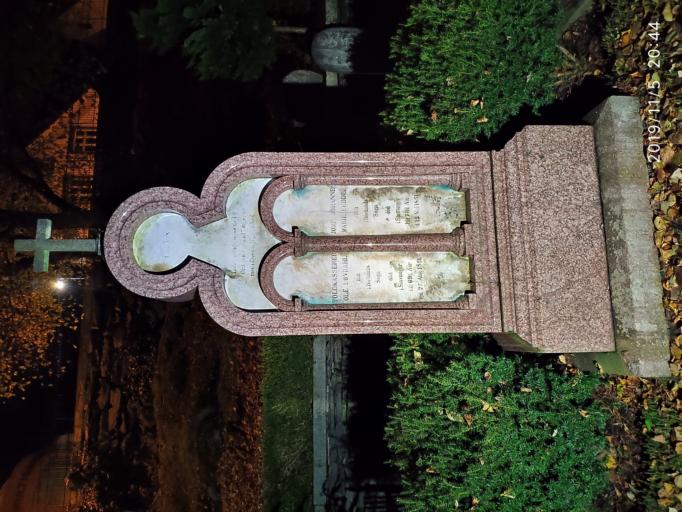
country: NO
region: Rogaland
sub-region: Stavanger
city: Stavanger
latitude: 58.9654
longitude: 5.7362
